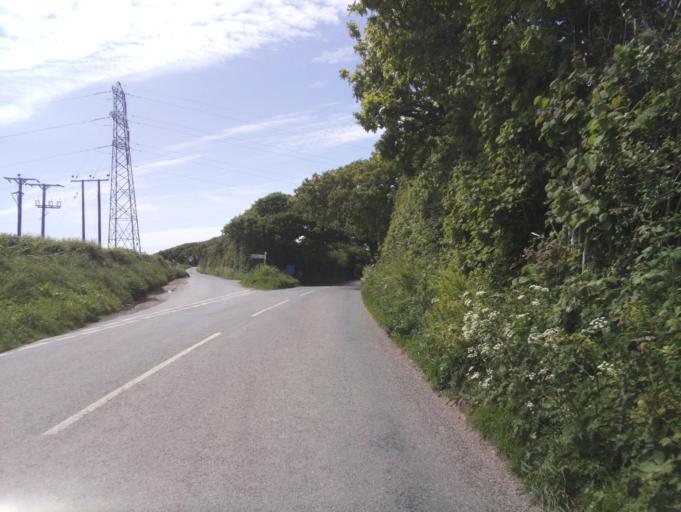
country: GB
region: England
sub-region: Devon
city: Kingsbridge
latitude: 50.3604
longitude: -3.7510
